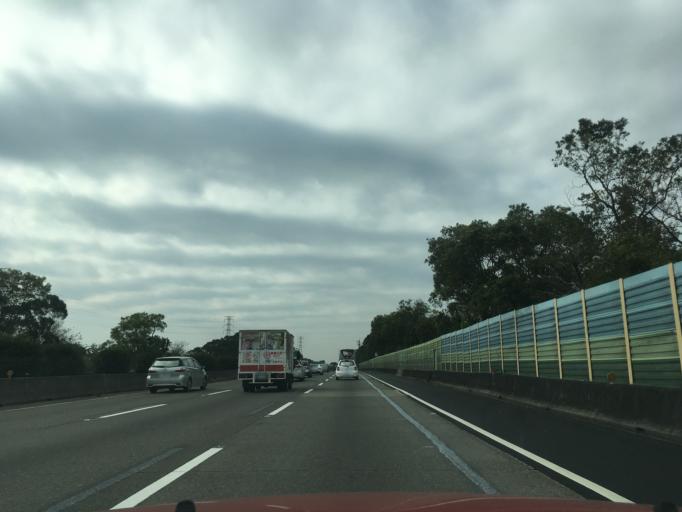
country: TW
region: Taiwan
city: Daxi
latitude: 24.8733
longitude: 121.2425
